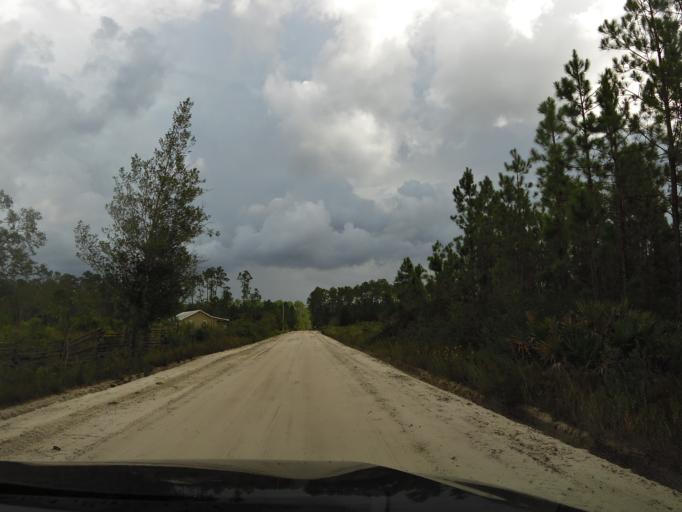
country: US
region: Florida
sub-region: Nassau County
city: Hilliard
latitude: 30.6125
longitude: -82.0795
